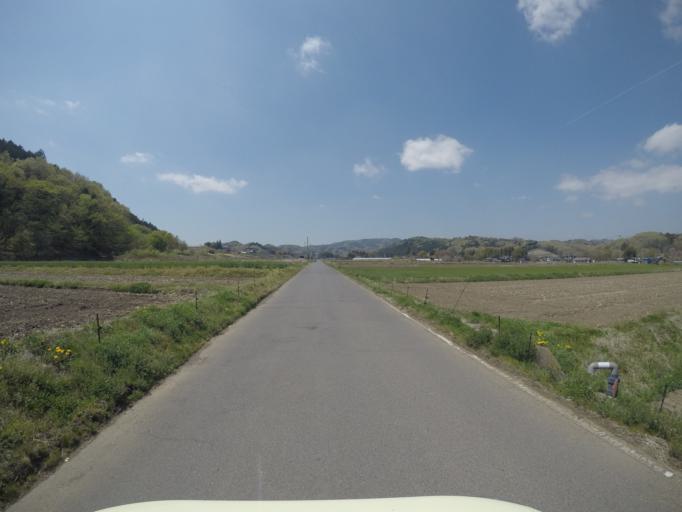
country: JP
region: Tochigi
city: Tochigi
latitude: 36.4523
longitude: 139.7025
